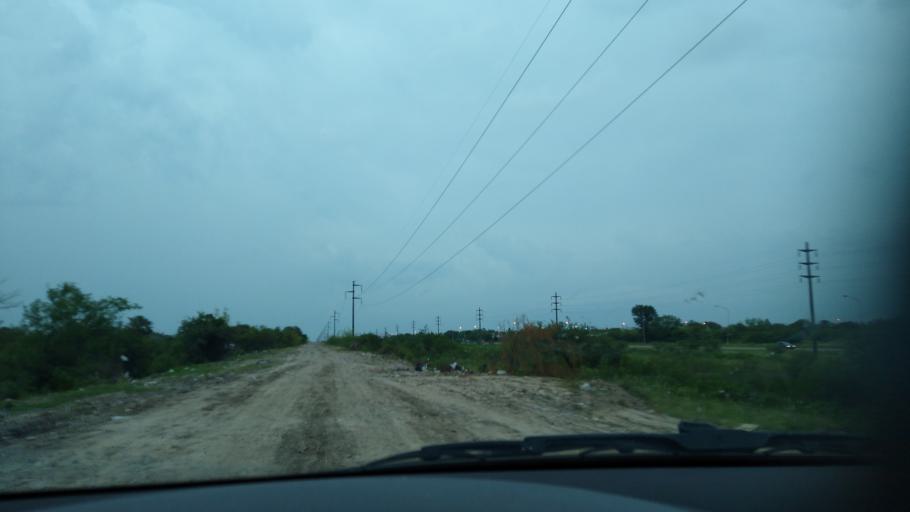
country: AR
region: Chaco
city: Puerto Vilelas
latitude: -27.5084
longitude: -58.9664
